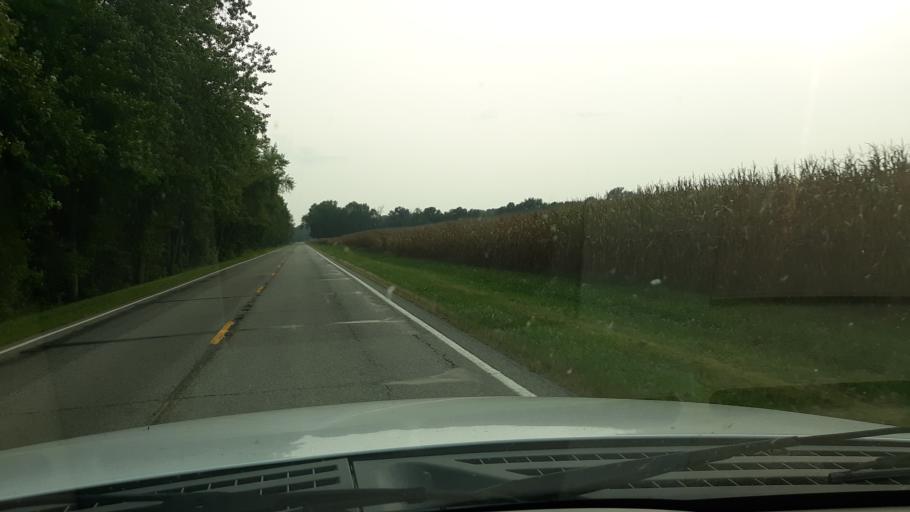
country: US
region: Illinois
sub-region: Edwards County
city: Grayville
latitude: 38.3052
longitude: -87.9457
